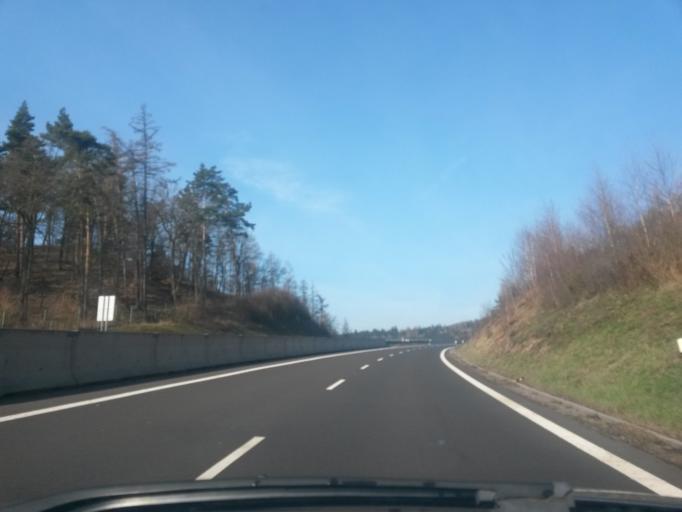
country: CZ
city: Krasna Lipa
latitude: 50.4705
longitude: 13.3638
